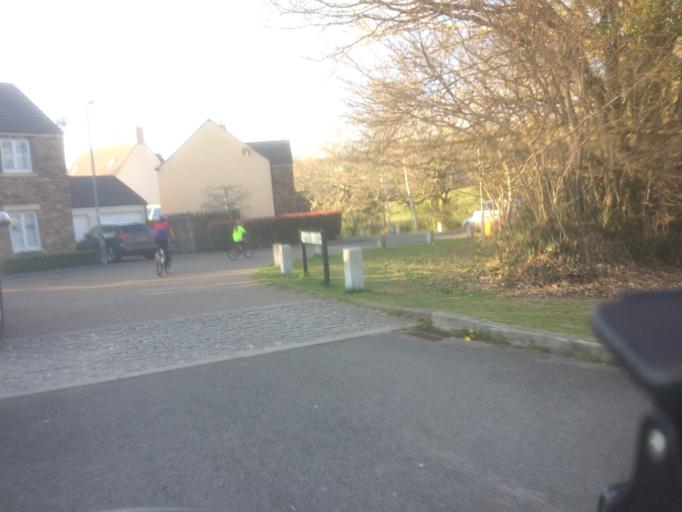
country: GB
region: England
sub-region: Devon
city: Tavistock
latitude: 50.5335
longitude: -4.1361
